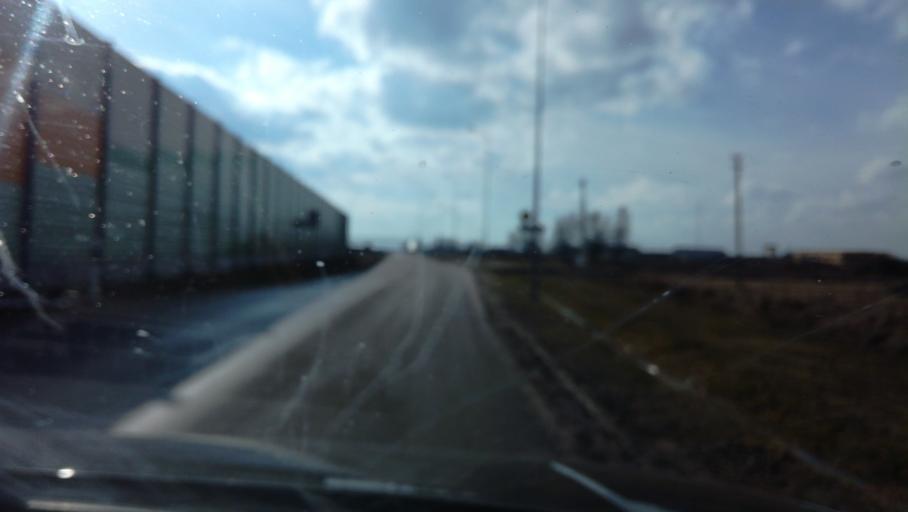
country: LT
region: Kauno apskritis
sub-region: Kauno rajonas
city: Mastaiciai
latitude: 54.8063
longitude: 23.8458
